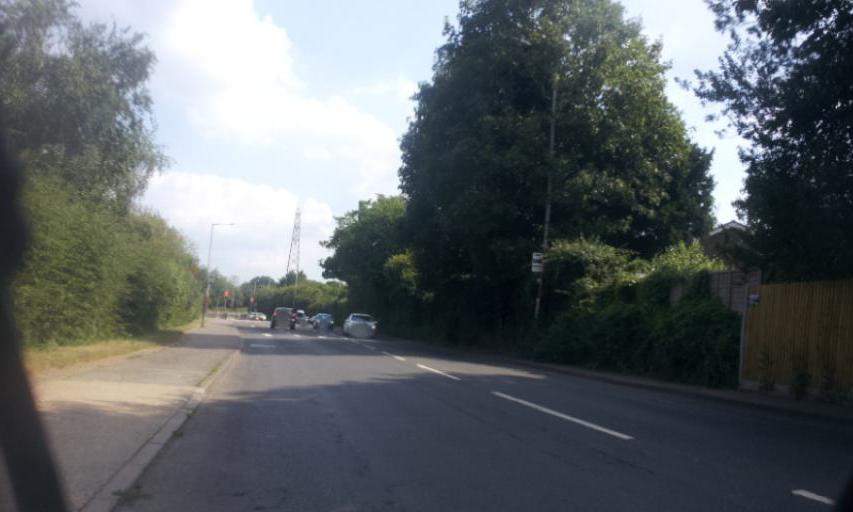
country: GB
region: England
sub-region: Kent
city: Paddock Wood
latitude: 51.1729
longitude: 0.3849
